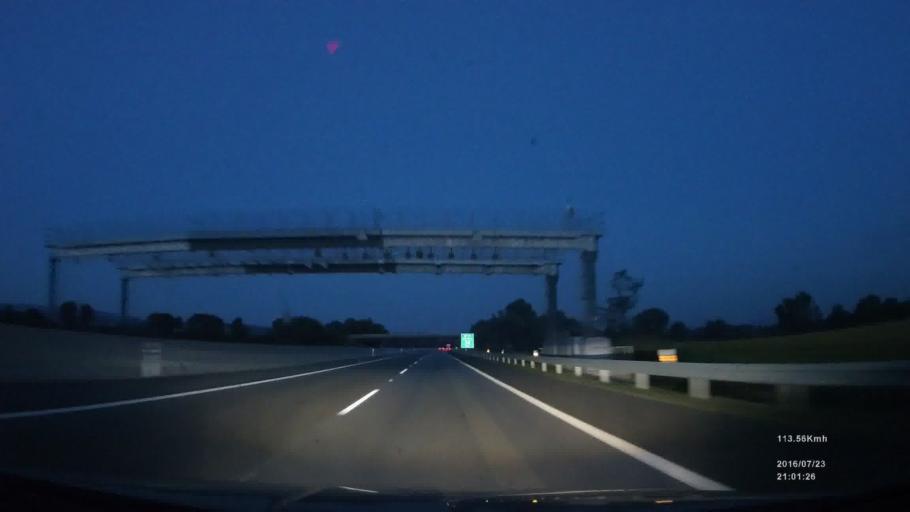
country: SK
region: Kosicky
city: Kosice
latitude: 48.8493
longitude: 21.2846
